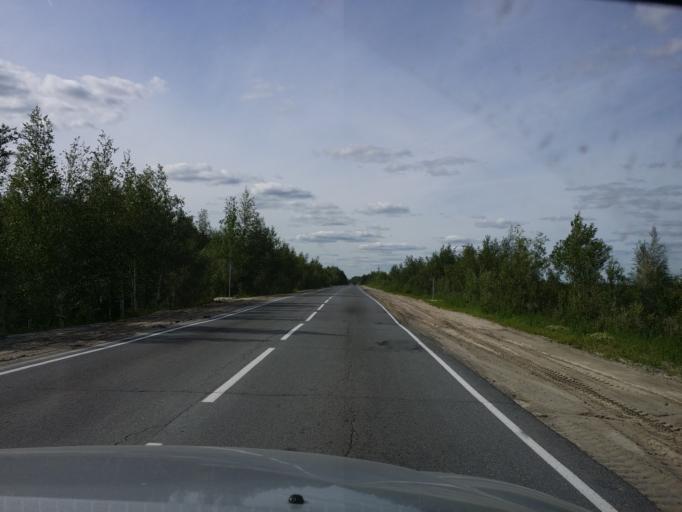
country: RU
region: Khanty-Mansiyskiy Avtonomnyy Okrug
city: Nizhnevartovsk
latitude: 61.1082
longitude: 76.6109
